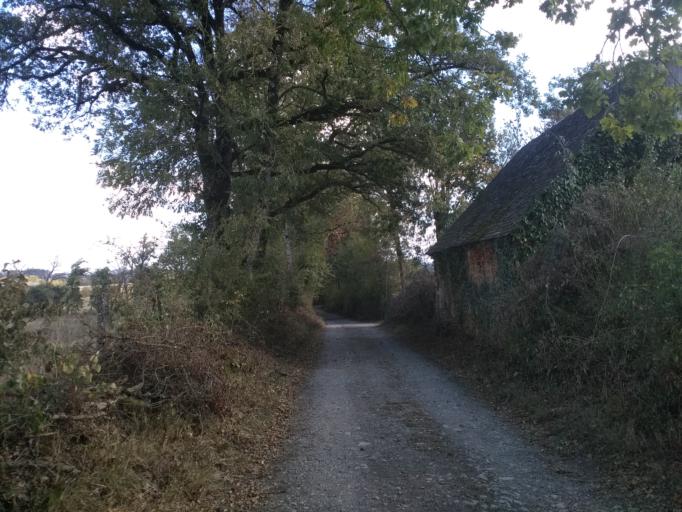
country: FR
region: Midi-Pyrenees
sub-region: Departement de l'Aveyron
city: Bozouls
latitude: 44.4761
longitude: 2.7061
